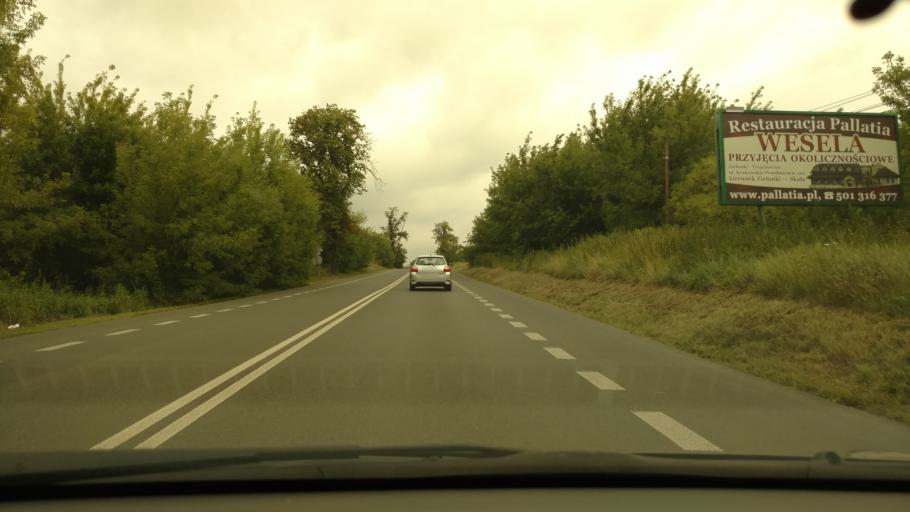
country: PL
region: Lesser Poland Voivodeship
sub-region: Powiat krakowski
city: Zielonki
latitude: 50.1023
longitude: 19.9636
